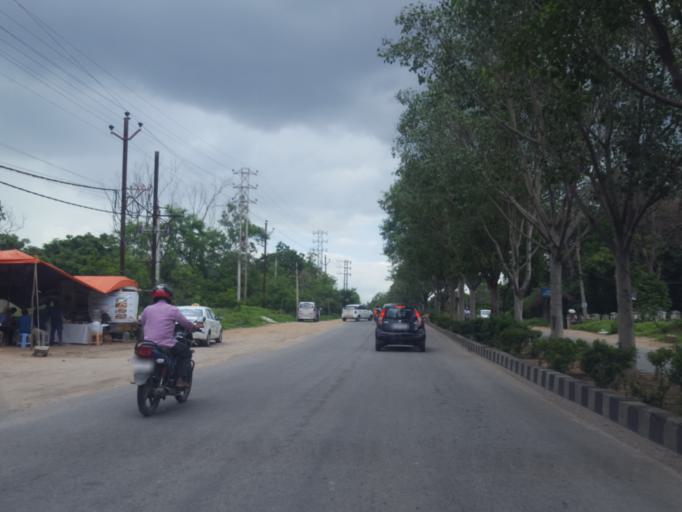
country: IN
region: Telangana
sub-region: Medak
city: Serilingampalle
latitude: 17.4622
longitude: 78.3354
